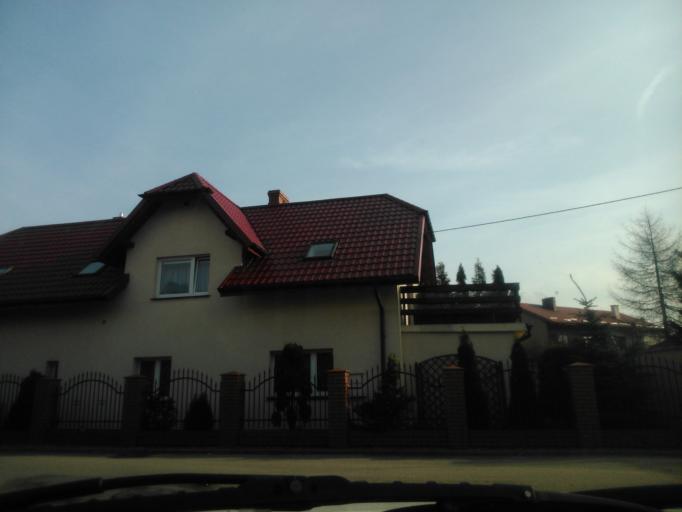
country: PL
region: Kujawsko-Pomorskie
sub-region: Powiat golubsko-dobrzynski
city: Golub-Dobrzyn
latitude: 53.1064
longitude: 19.0578
